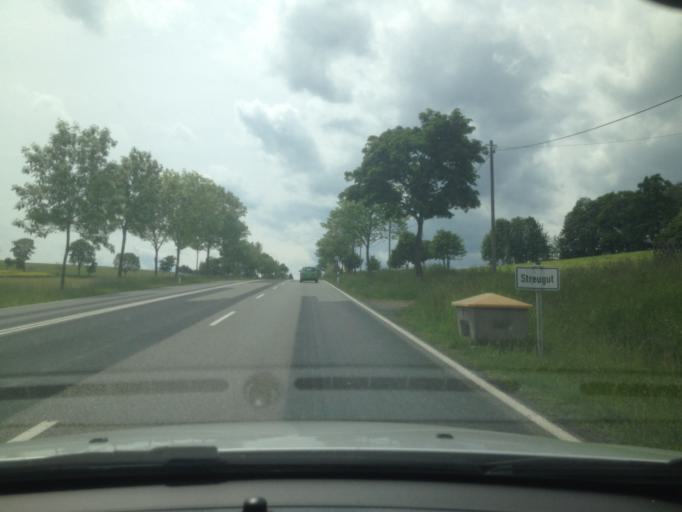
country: DE
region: Saxony
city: Lossnitz
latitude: 50.6637
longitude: 12.7583
